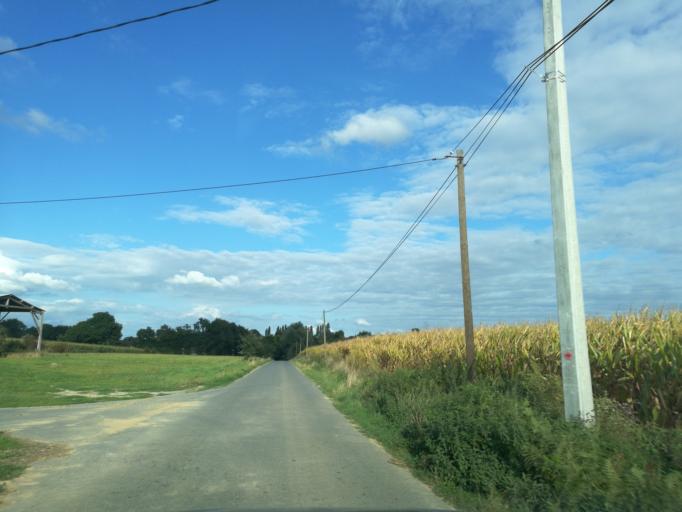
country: FR
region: Brittany
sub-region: Departement d'Ille-et-Vilaine
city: Montfort-sur-Meu
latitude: 48.1508
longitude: -1.9373
